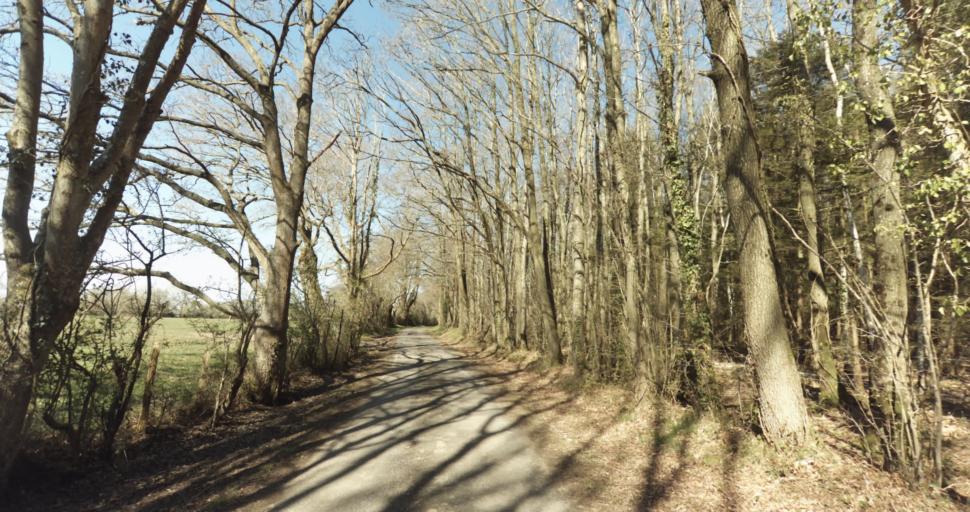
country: FR
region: Lower Normandy
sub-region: Departement du Calvados
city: Livarot
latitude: 49.0235
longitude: 0.0948
